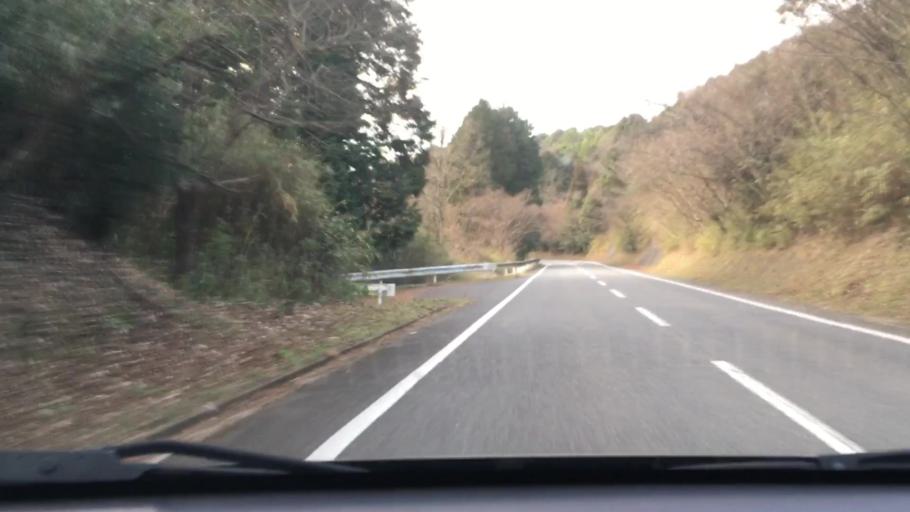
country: JP
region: Oita
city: Hiji
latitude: 33.4122
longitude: 131.4243
